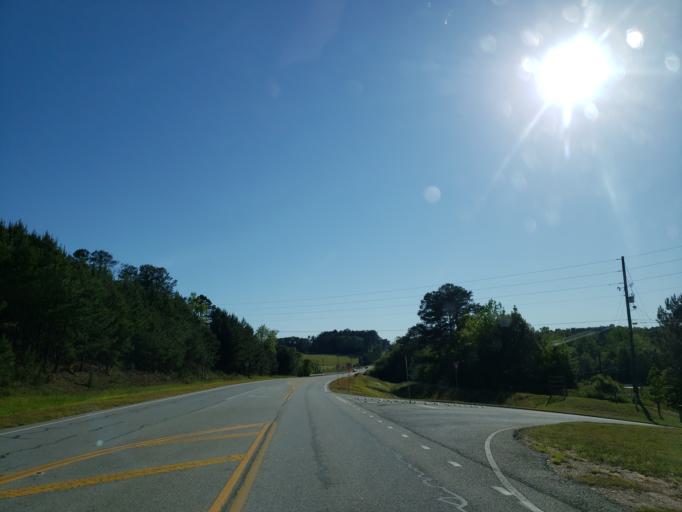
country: US
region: Georgia
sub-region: Haralson County
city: Buchanan
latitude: 33.8112
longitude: -85.1415
